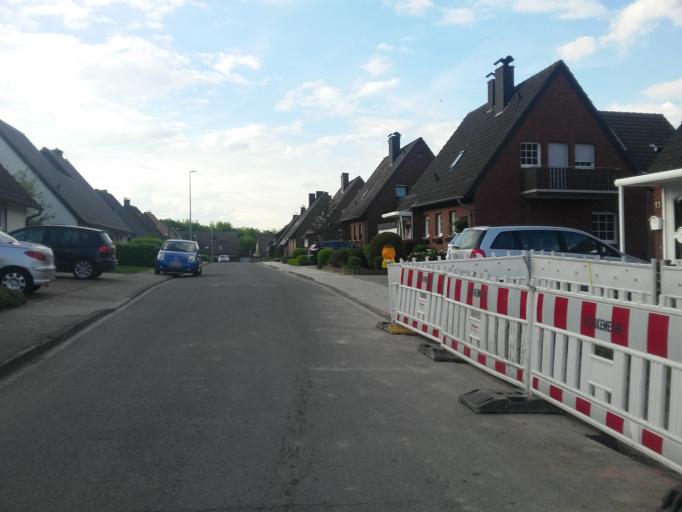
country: DE
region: North Rhine-Westphalia
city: Ahlen
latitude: 51.7431
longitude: 7.8771
